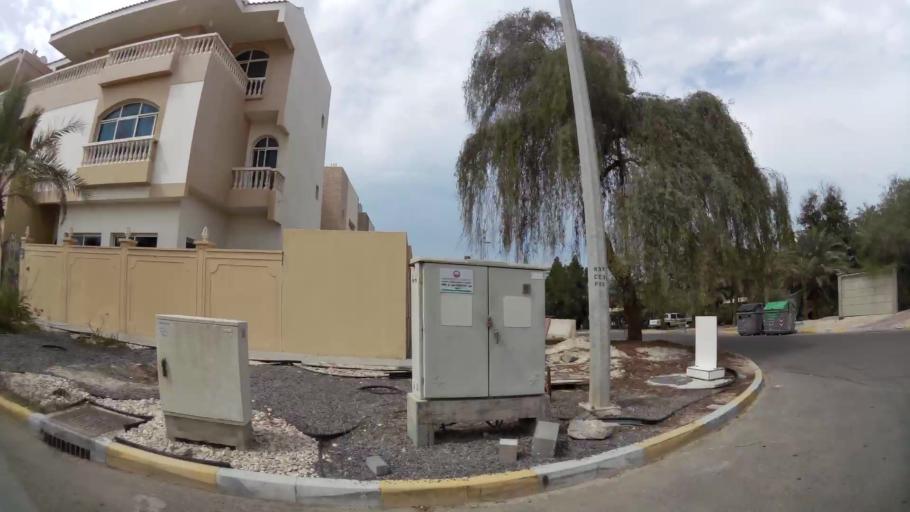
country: AE
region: Abu Dhabi
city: Abu Dhabi
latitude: 24.4637
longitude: 54.3378
